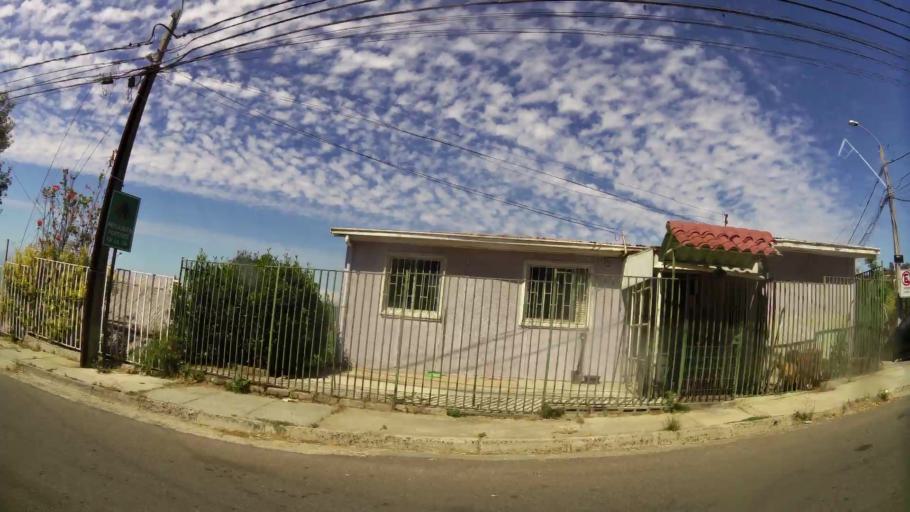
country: CL
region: Valparaiso
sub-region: Provincia de Valparaiso
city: Vina del Mar
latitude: -33.0387
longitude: -71.5769
